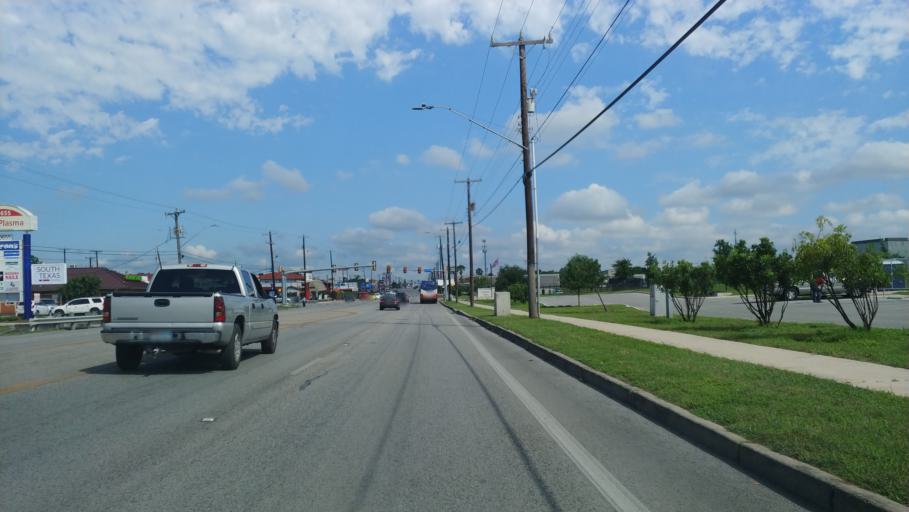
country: US
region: Texas
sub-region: Bexar County
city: Balcones Heights
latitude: 29.4789
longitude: -98.5402
